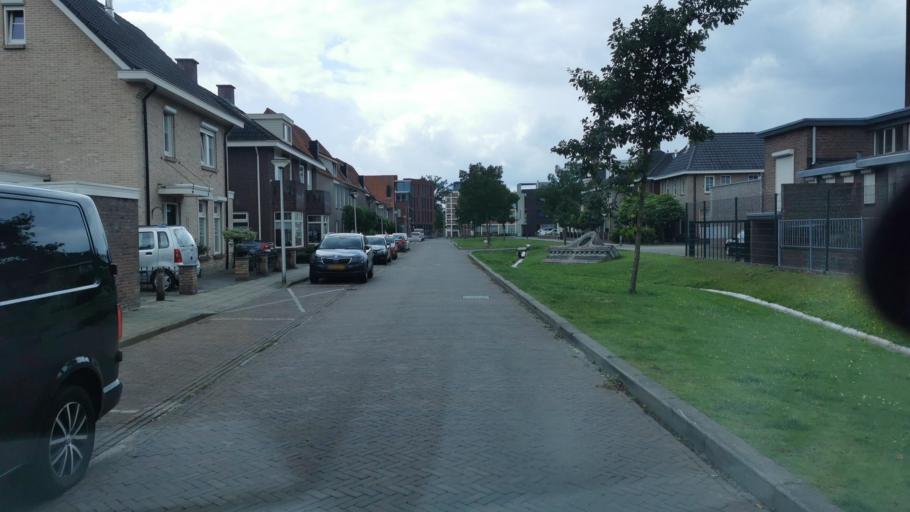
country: NL
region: Overijssel
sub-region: Gemeente Enschede
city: Enschede
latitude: 52.2336
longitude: 6.8997
